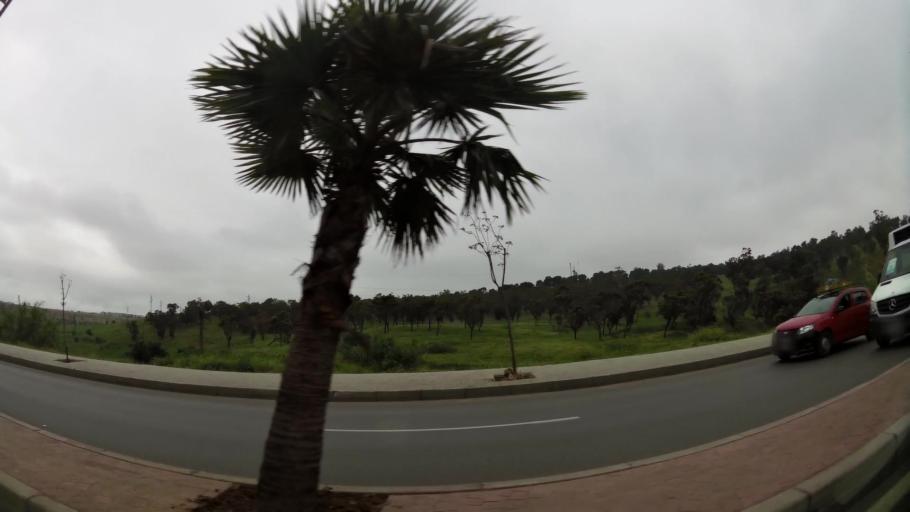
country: MA
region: Fes-Boulemane
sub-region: Fes
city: Fes
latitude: 34.0521
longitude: -4.9830
